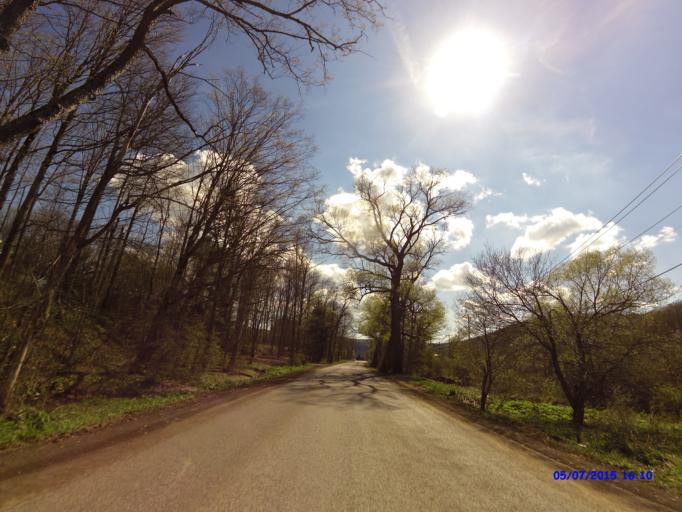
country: US
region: New York
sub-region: Cattaraugus County
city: Salamanca
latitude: 42.2661
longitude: -78.6285
